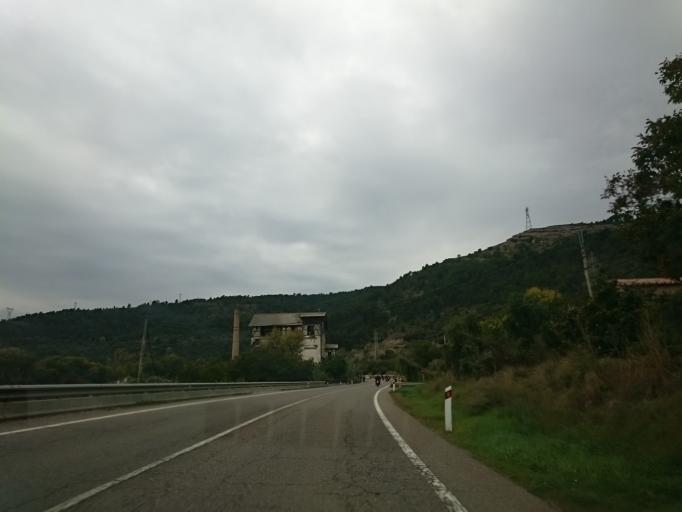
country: ES
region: Catalonia
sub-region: Provincia de Lleida
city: Senterada
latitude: 42.2600
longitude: 0.9837
